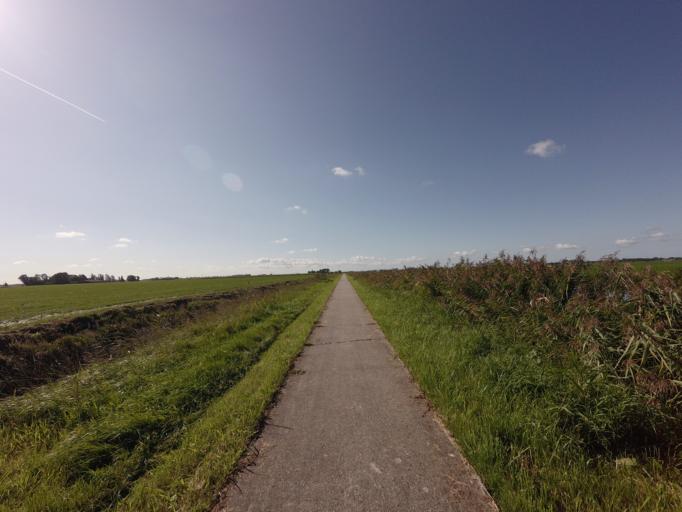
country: NL
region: Friesland
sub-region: Gemeente Boarnsterhim
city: Reduzum
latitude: 53.1368
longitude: 5.7600
